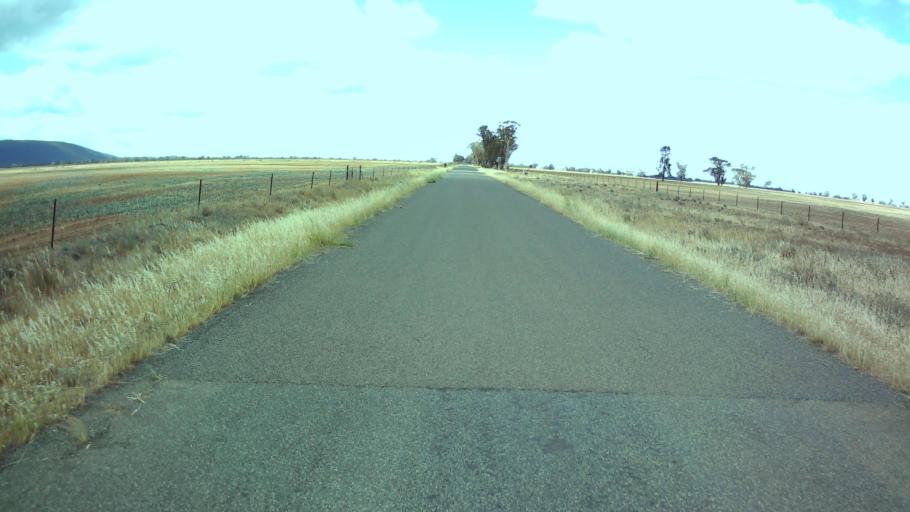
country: AU
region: New South Wales
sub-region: Weddin
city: Grenfell
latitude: -33.8697
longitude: 147.9267
